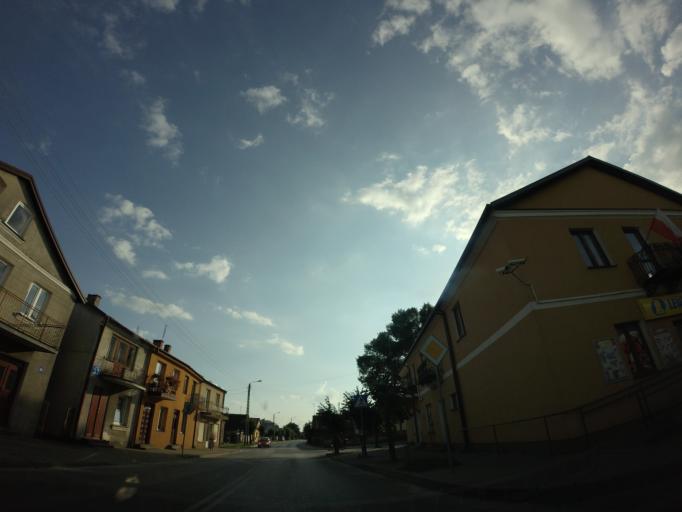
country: PL
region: Lublin Voivodeship
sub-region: Powiat lubartowski
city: Michow
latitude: 51.5231
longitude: 22.3131
